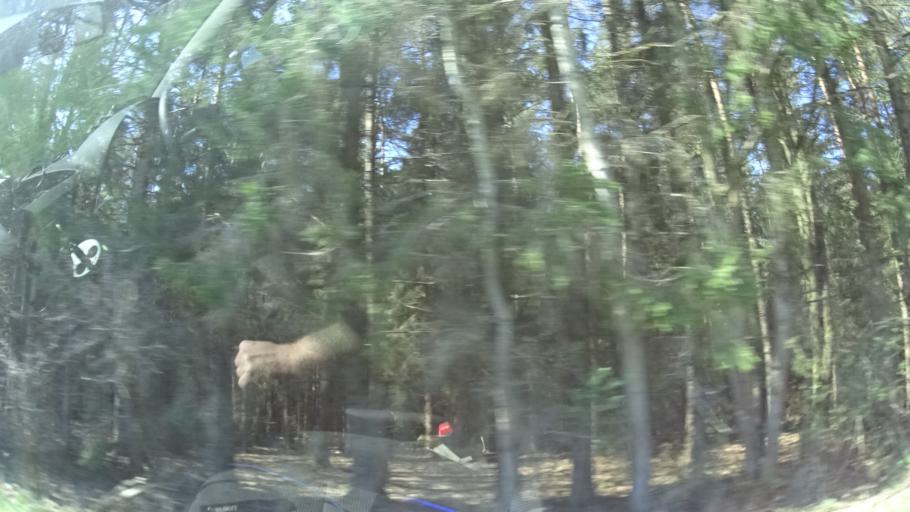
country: DE
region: Bavaria
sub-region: Regierungsbezirk Mittelfranken
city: Alfeld
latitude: 49.4171
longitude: 11.5642
